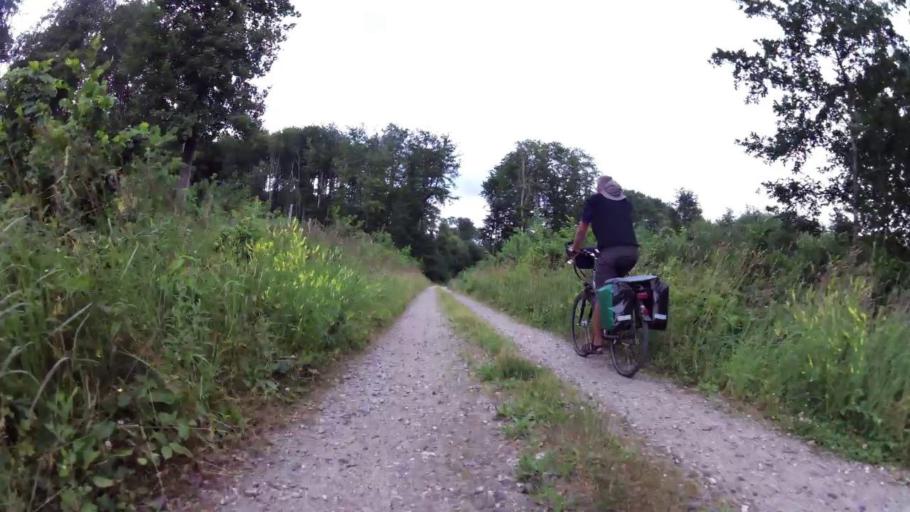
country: PL
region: West Pomeranian Voivodeship
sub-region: Powiat lobeski
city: Lobez
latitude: 53.7595
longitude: 15.5904
